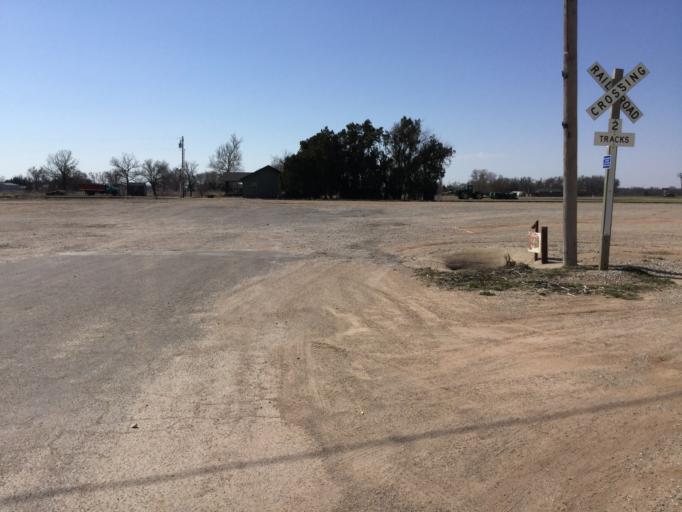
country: US
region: Kansas
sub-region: Barber County
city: Medicine Lodge
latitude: 37.2473
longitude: -98.4203
